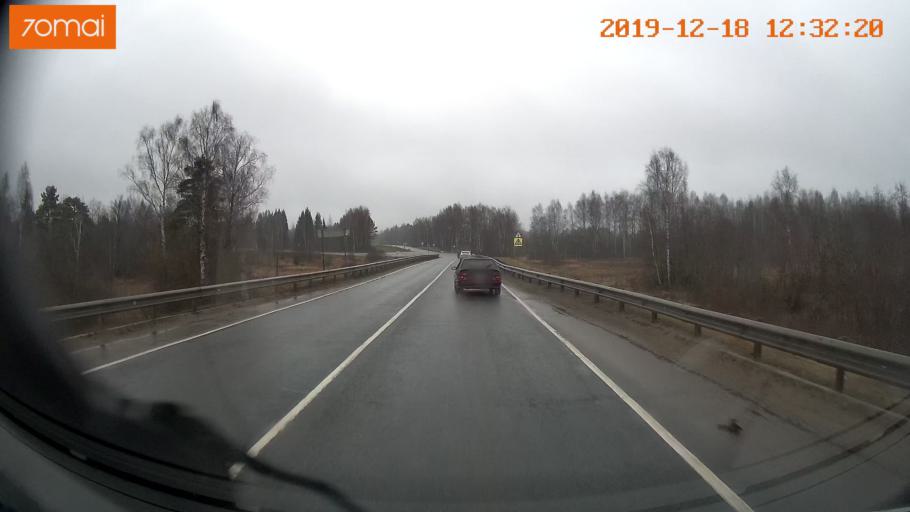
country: RU
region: Moskovskaya
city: Rumyantsevo
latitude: 56.1051
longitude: 36.5497
